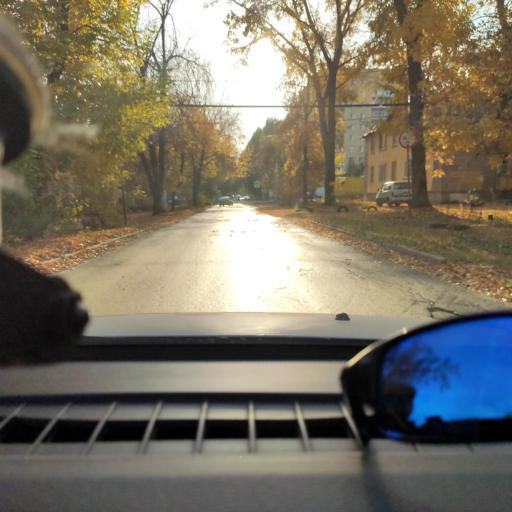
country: RU
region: Samara
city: Samara
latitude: 53.2394
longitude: 50.2565
